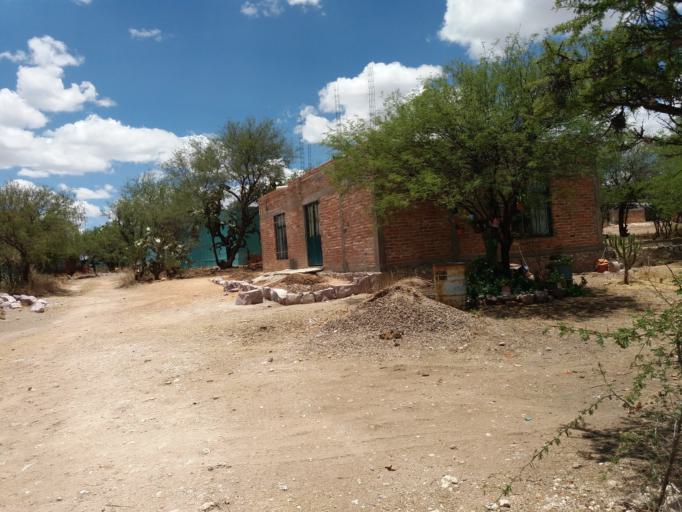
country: MX
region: Aguascalientes
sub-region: Aguascalientes
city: San Sebastian [Fraccionamiento]
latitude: 21.7783
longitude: -102.2591
